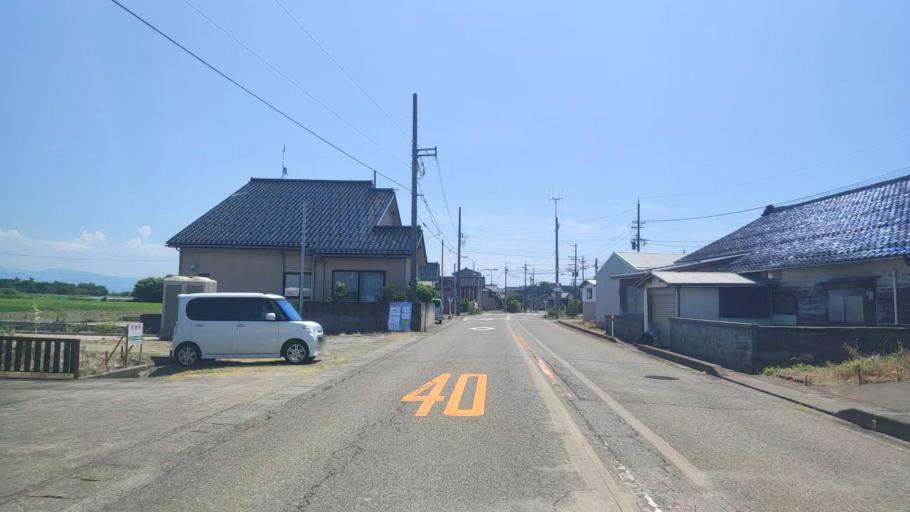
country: JP
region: Ishikawa
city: Kanazawa-shi
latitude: 36.6651
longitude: 136.6583
